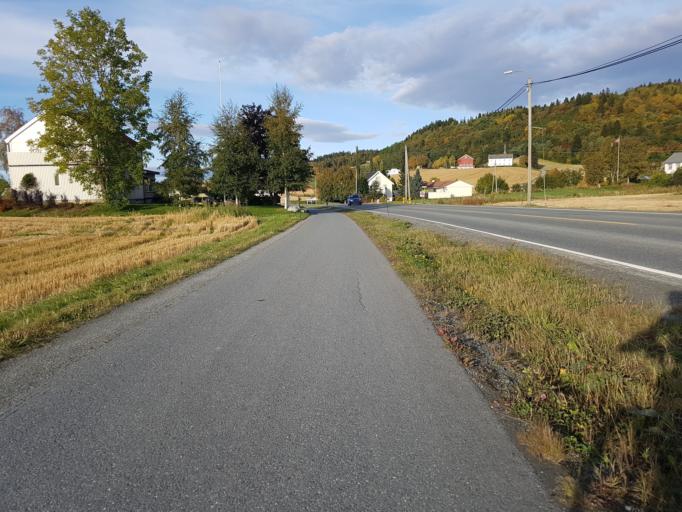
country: NO
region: Sor-Trondelag
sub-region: Trondheim
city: Trondheim
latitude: 63.3781
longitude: 10.4335
